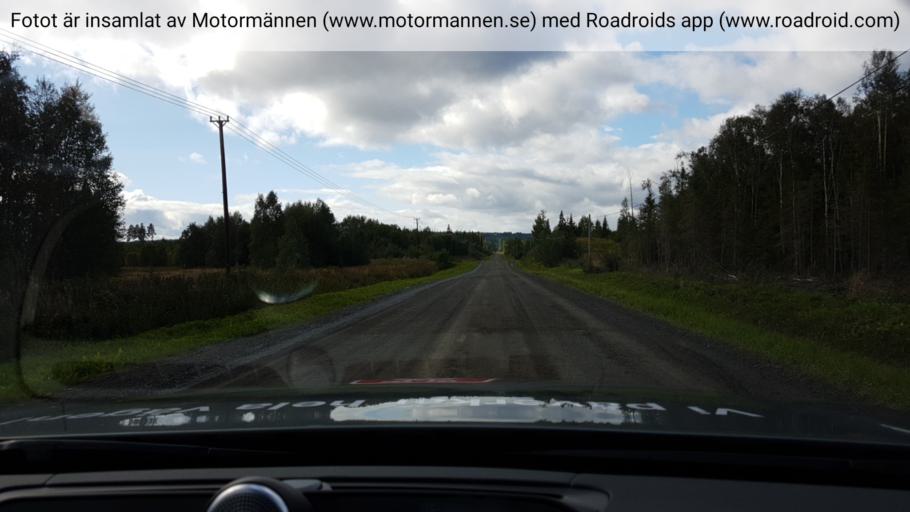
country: SE
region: Jaemtland
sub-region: Stroemsunds Kommun
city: Stroemsund
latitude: 63.6241
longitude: 15.1788
